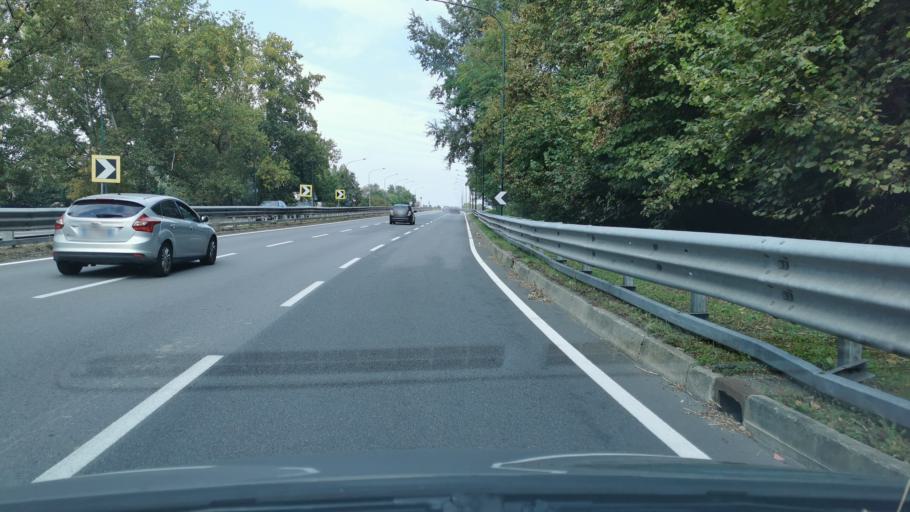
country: IT
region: Piedmont
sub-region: Provincia di Torino
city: San Mauro Torinese
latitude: 45.0897
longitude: 7.7275
